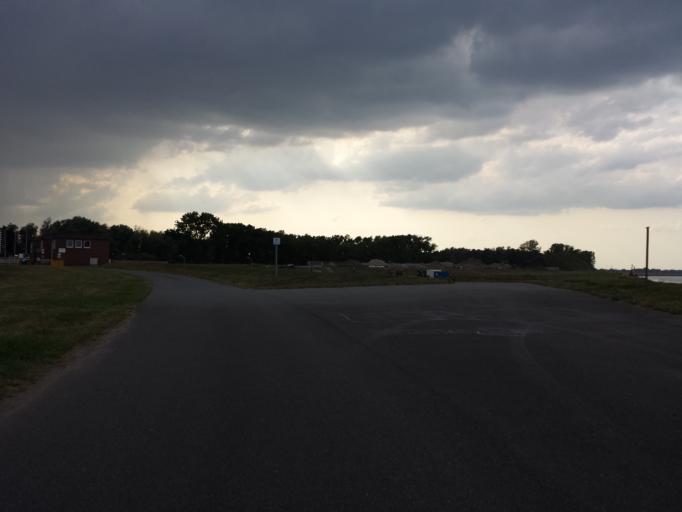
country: DE
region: Lower Saxony
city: Lemwerder
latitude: 53.1234
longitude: 8.6514
